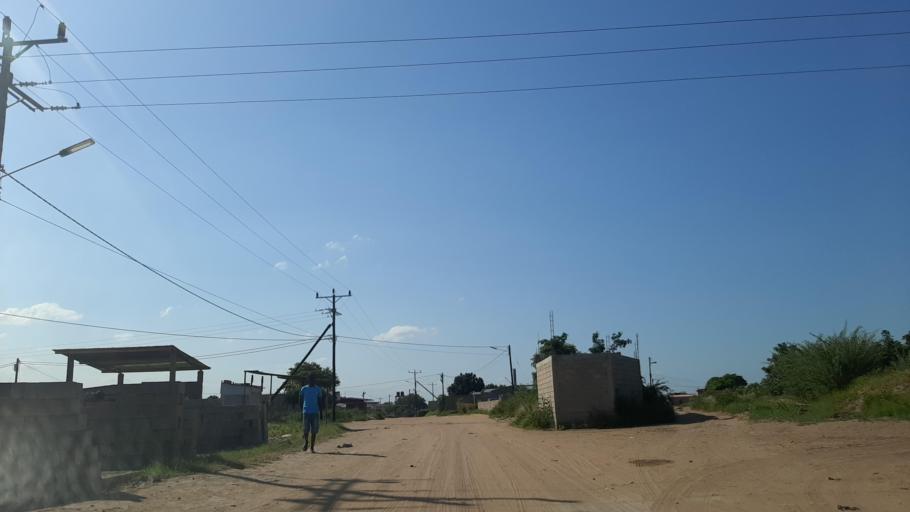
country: MZ
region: Maputo
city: Matola
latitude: -25.7953
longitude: 32.4895
